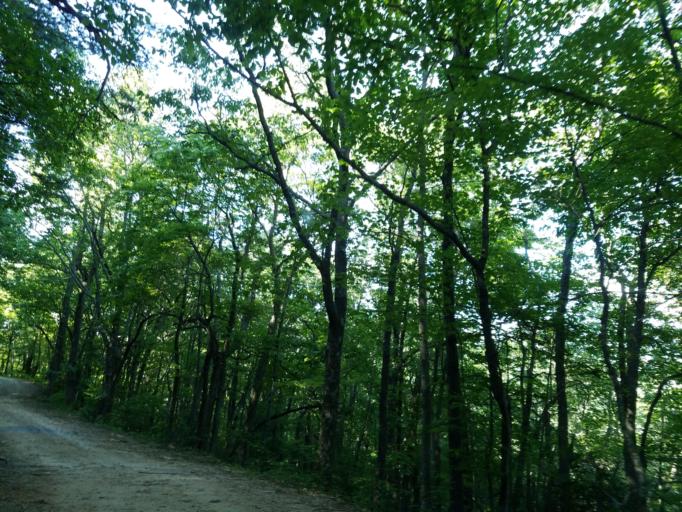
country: US
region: Georgia
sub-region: Dawson County
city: Dawsonville
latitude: 34.6021
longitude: -84.2116
